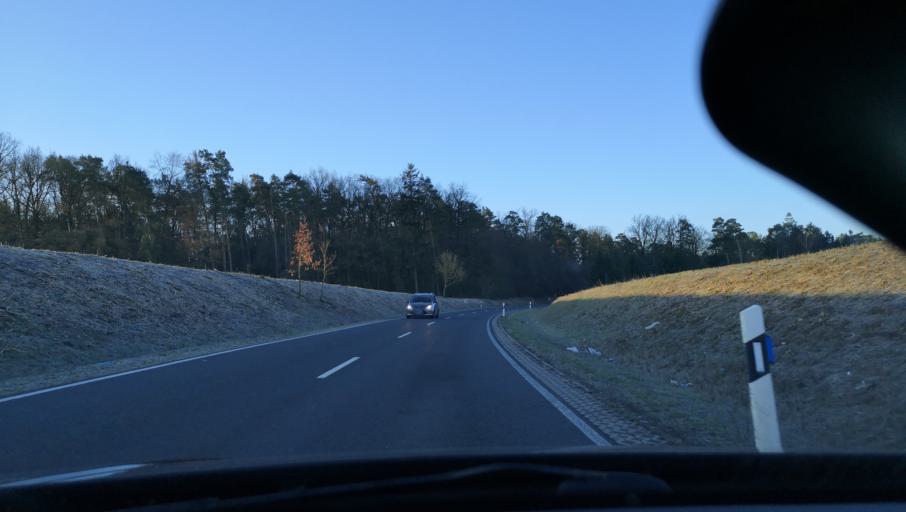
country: DE
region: Bavaria
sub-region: Upper Franconia
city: Rodental
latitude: 50.2715
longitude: 11.0959
